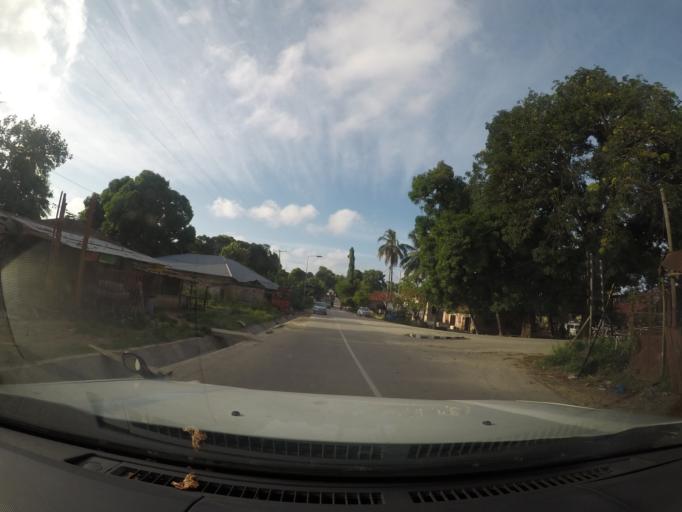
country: TZ
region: Pemba South
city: Chake Chake
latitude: -5.2437
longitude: 39.7824
